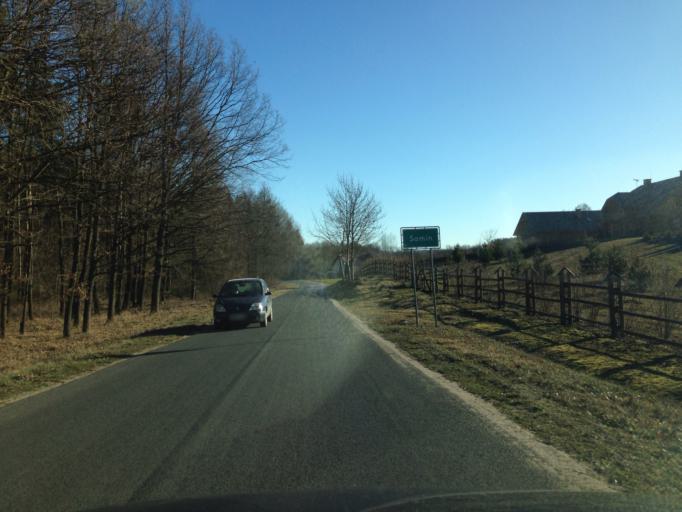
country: PL
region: Kujawsko-Pomorskie
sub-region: Powiat brodnicki
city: Bartniczka
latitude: 53.2667
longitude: 19.6418
